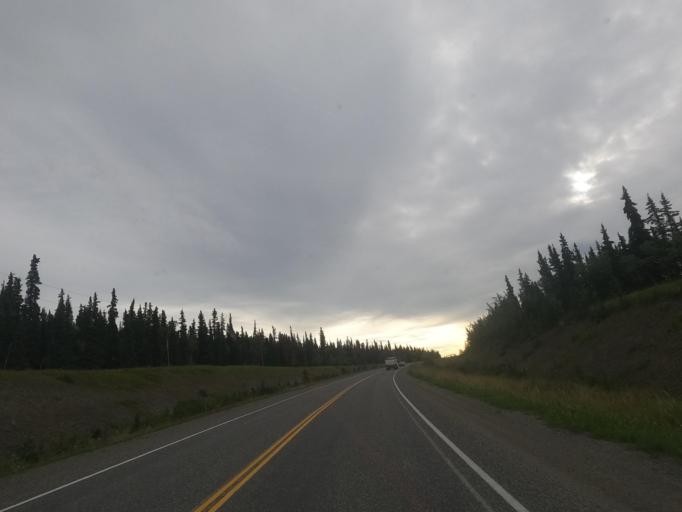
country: CA
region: Yukon
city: Whitehorse
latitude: 60.7650
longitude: -136.0985
